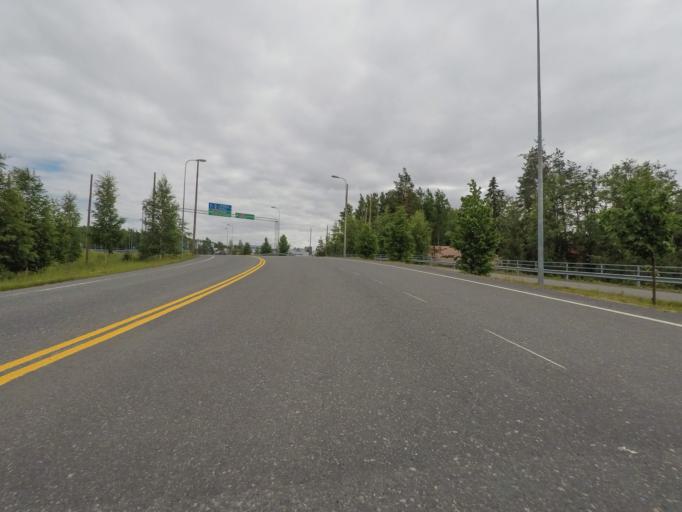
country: FI
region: Northern Savo
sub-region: Kuopio
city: Kuopio
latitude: 62.9733
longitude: 27.7030
